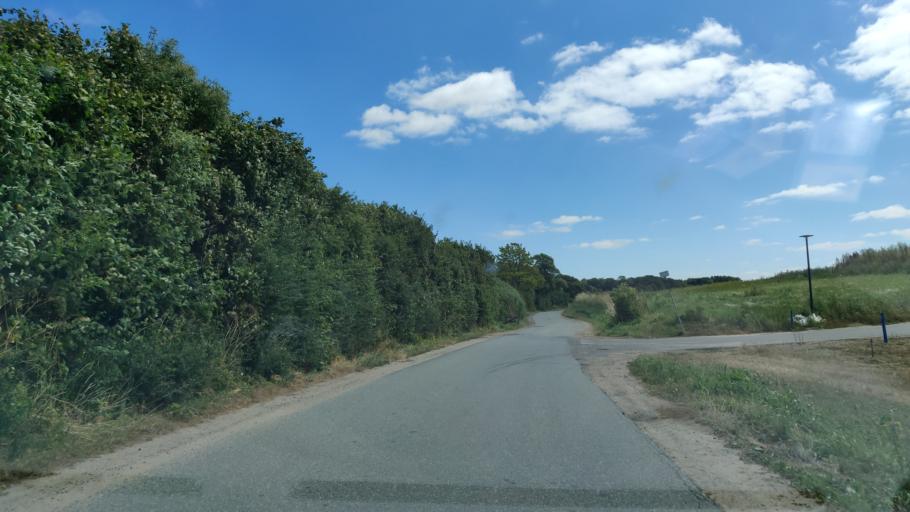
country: DK
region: South Denmark
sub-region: Fredericia Kommune
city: Taulov
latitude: 55.5249
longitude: 9.5446
